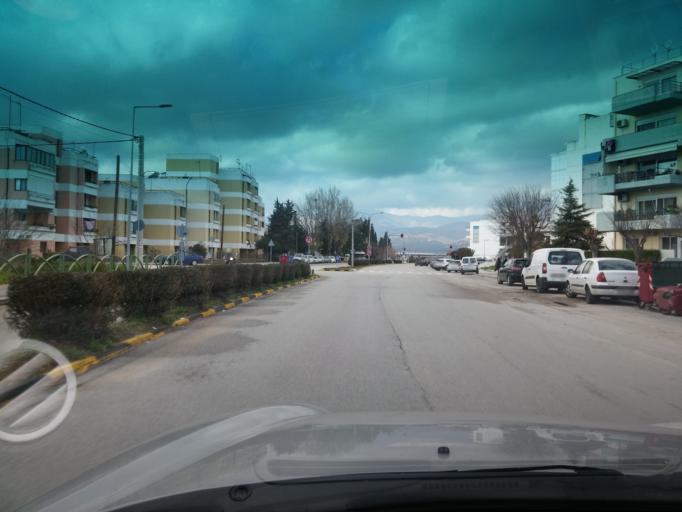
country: GR
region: East Macedonia and Thrace
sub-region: Nomos Rodopis
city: Komotini
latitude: 41.1239
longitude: 25.3953
